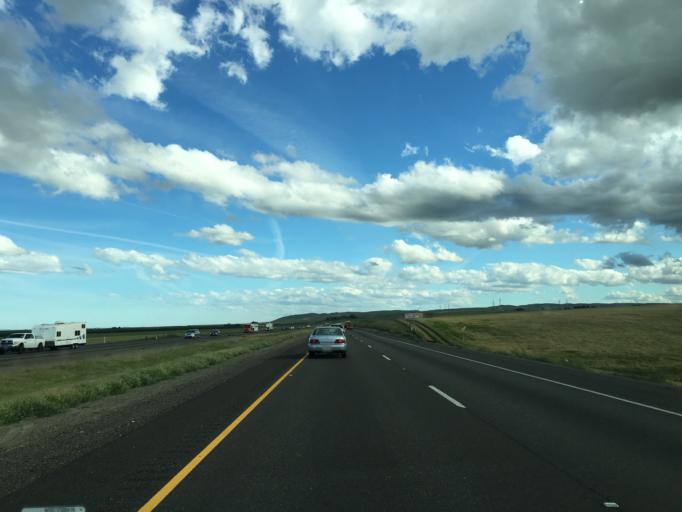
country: US
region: California
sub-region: Merced County
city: Los Banos
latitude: 36.9872
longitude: -120.9041
